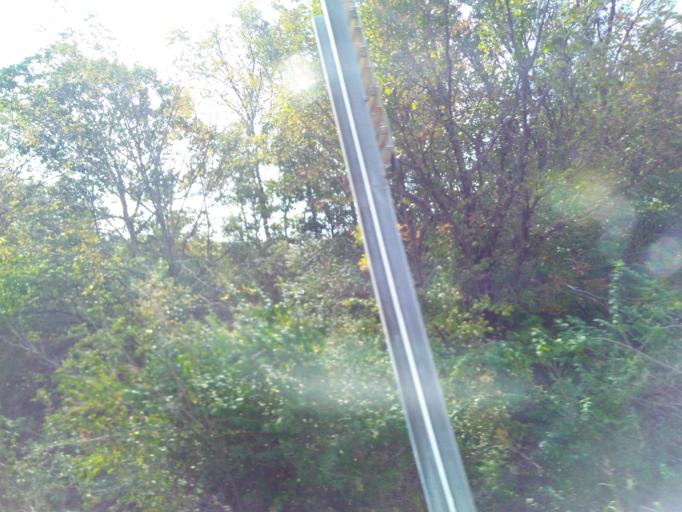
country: US
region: Missouri
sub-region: Saint Louis County
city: Concord
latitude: 38.5134
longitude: -90.3740
